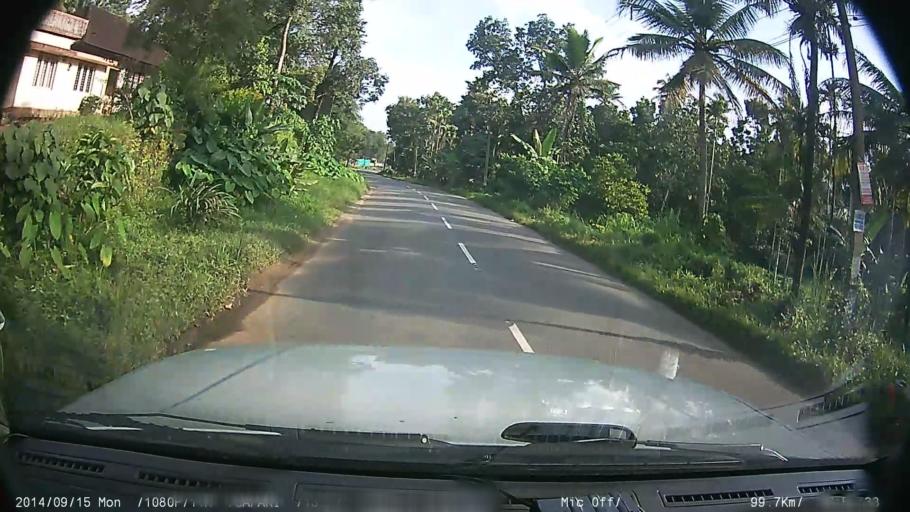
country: IN
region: Kerala
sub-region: Ernakulam
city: Piravam
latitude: 9.8467
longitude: 76.5912
